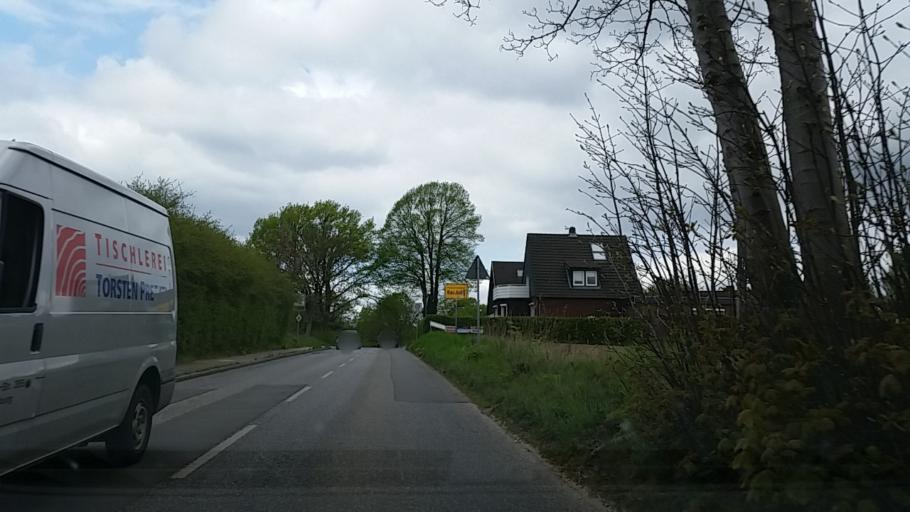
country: DE
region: Hamburg
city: Harburg
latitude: 53.4325
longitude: 10.0131
